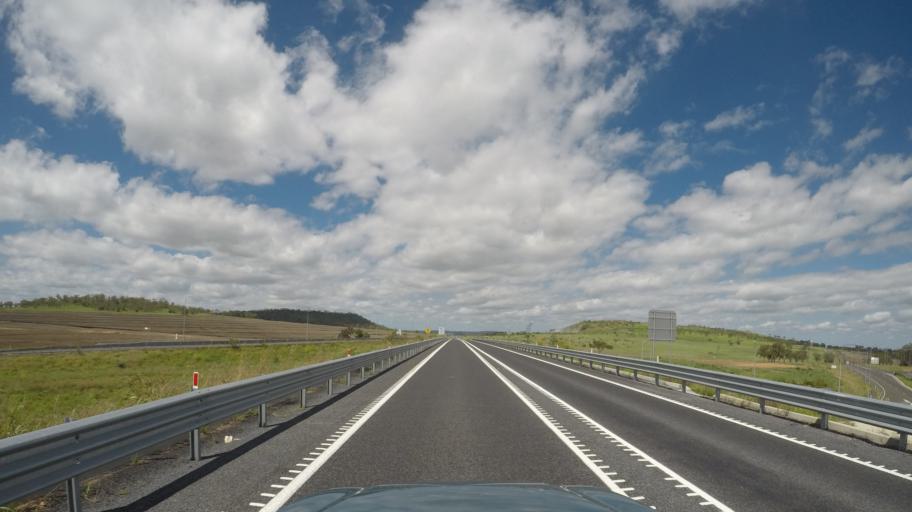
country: AU
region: Queensland
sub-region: Toowoomba
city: Westbrook
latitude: -27.5474
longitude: 151.8334
